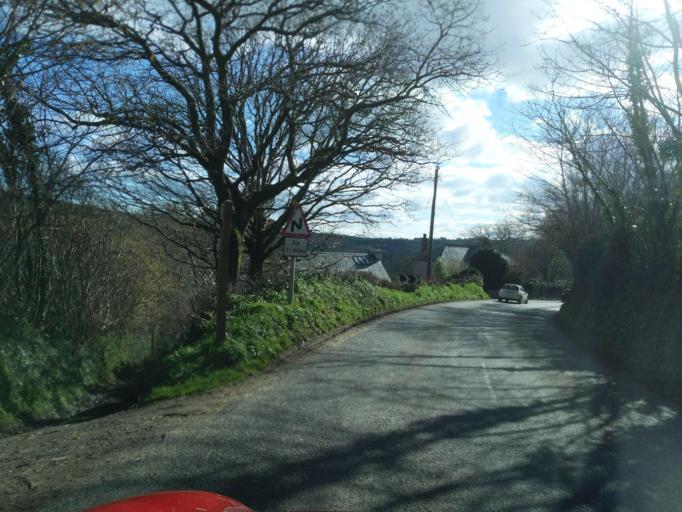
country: GB
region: England
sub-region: Devon
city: Kingsbridge
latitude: 50.3200
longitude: -3.7983
